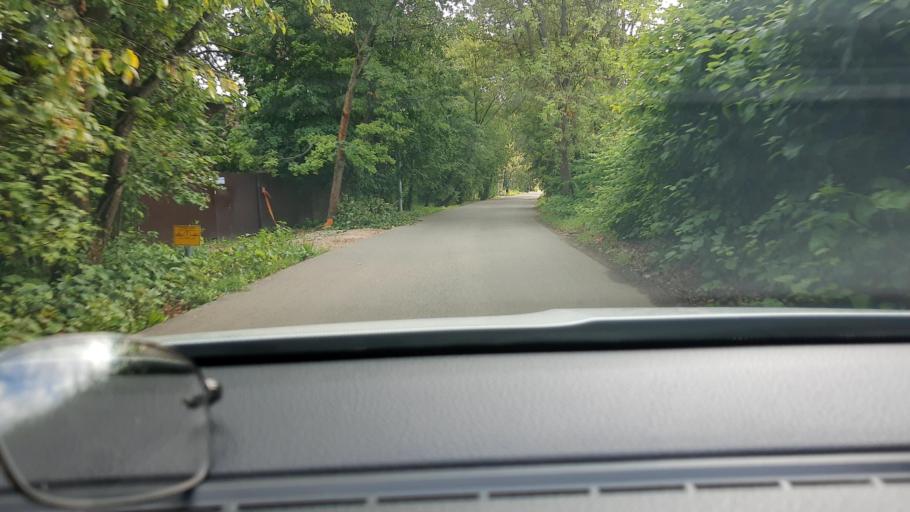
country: RU
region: Moskovskaya
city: Kokoshkino
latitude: 55.5969
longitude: 37.1668
